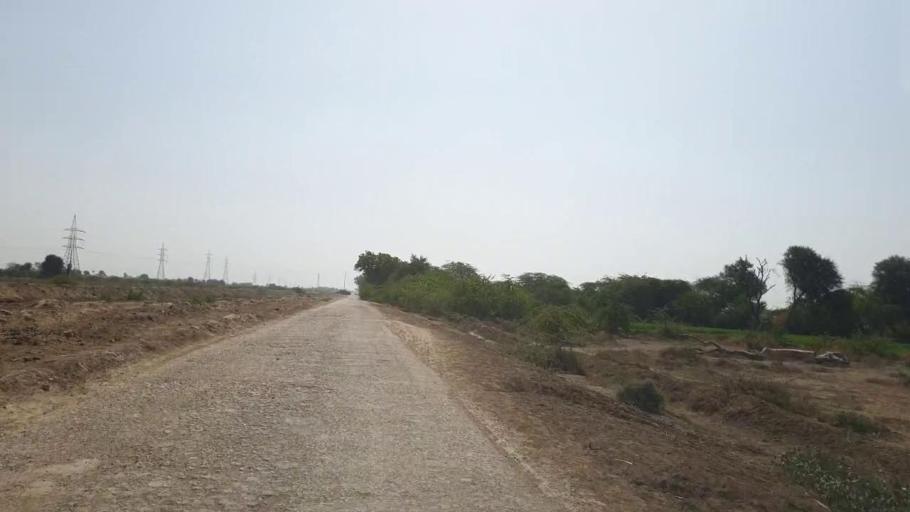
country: PK
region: Sindh
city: Naukot
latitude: 25.0106
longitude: 69.4579
